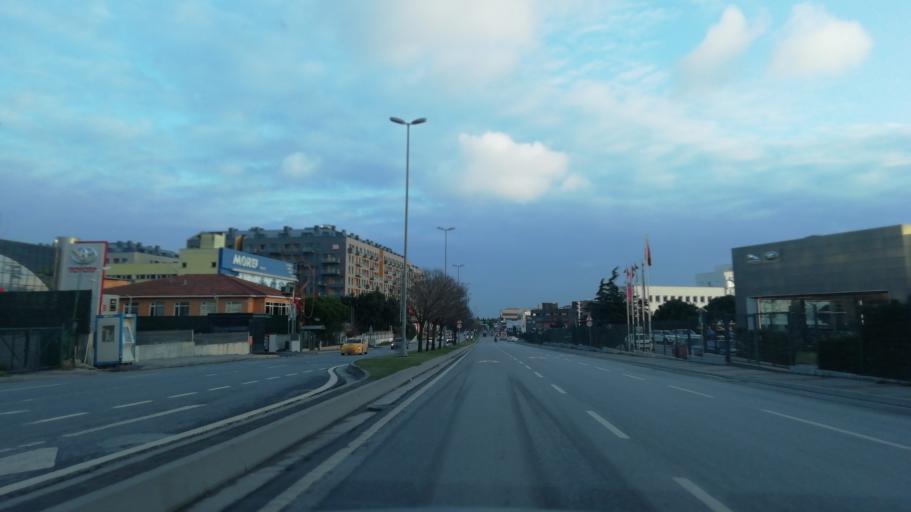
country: TR
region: Istanbul
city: Yakuplu
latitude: 40.9942
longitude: 28.7162
